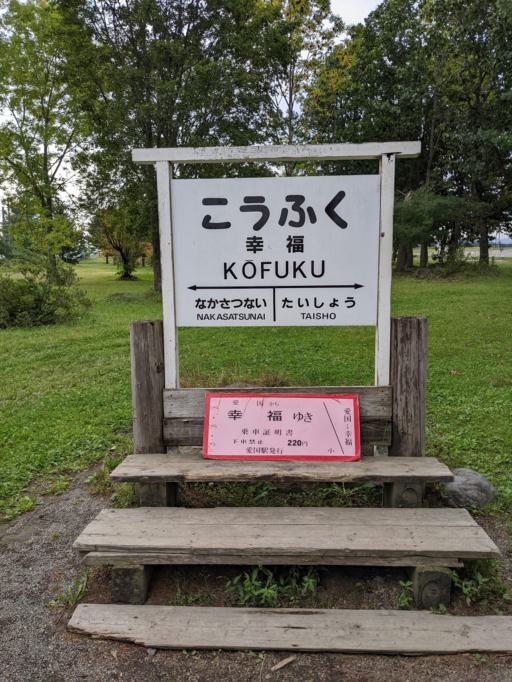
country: JP
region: Hokkaido
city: Obihiro
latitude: 42.7451
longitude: 143.1617
